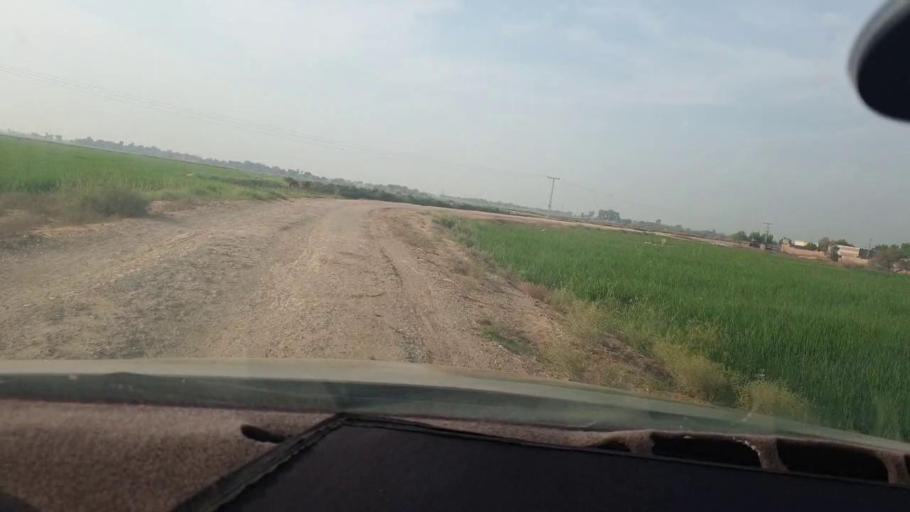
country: PK
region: Balochistan
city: Jhatpat
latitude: 28.3328
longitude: 68.3957
